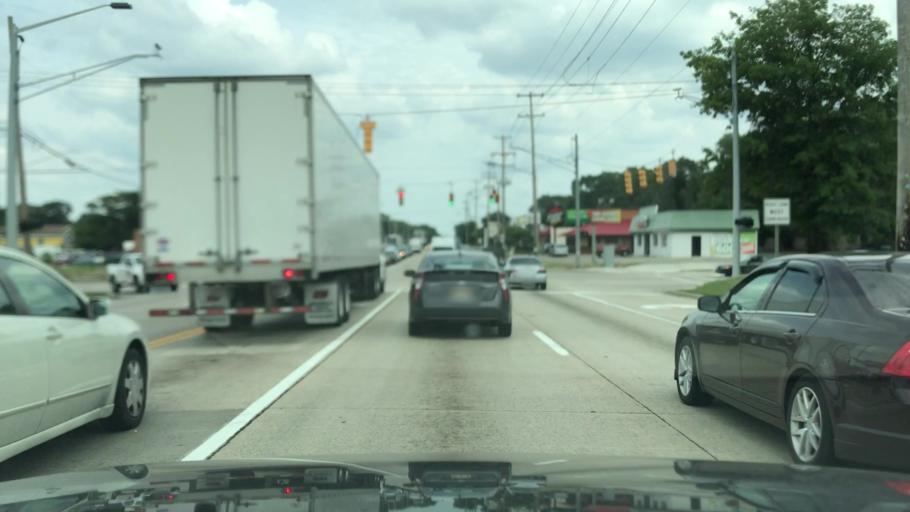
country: US
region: Michigan
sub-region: Kent County
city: Wyoming
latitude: 42.9131
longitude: -85.6716
